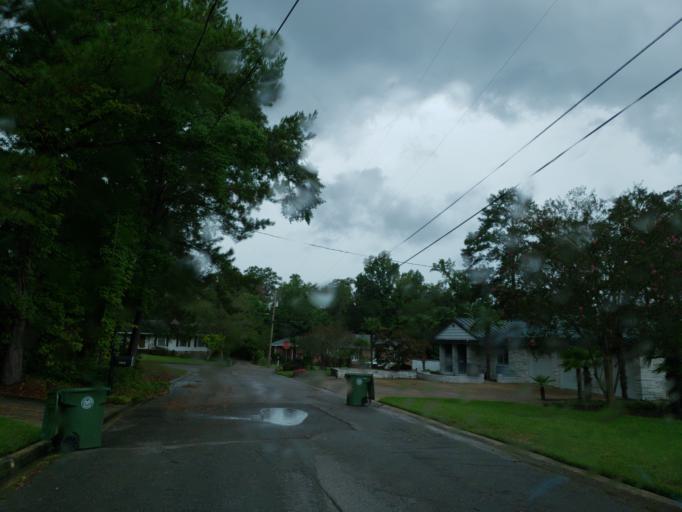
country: US
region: Mississippi
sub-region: Lamar County
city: West Hattiesburg
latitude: 31.3152
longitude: -89.3331
